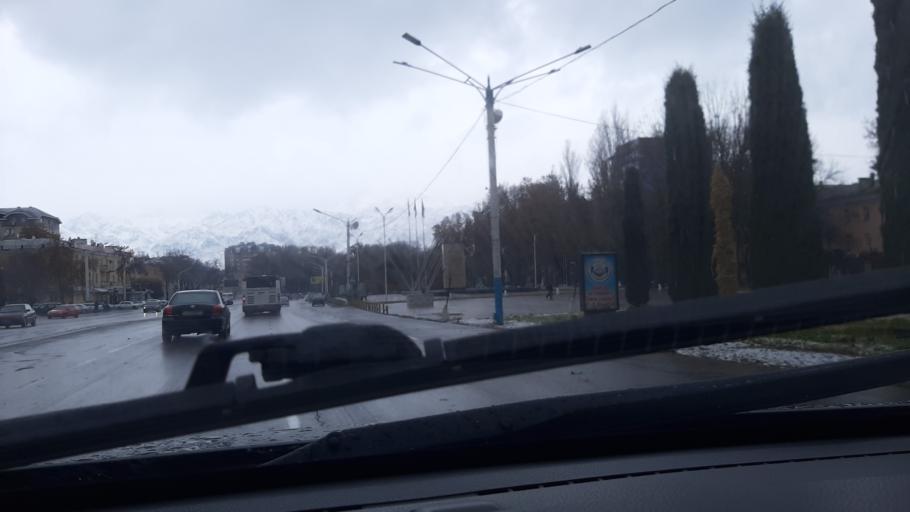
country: TJ
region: Viloyati Sughd
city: Khujand
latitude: 40.2830
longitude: 69.6240
